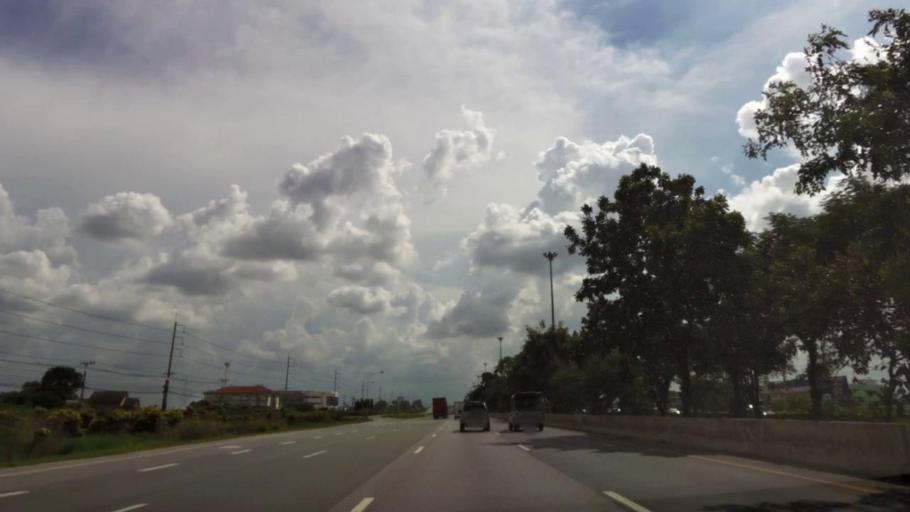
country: TH
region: Phra Nakhon Si Ayutthaya
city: Bang Pa-in
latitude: 14.2821
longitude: 100.6135
